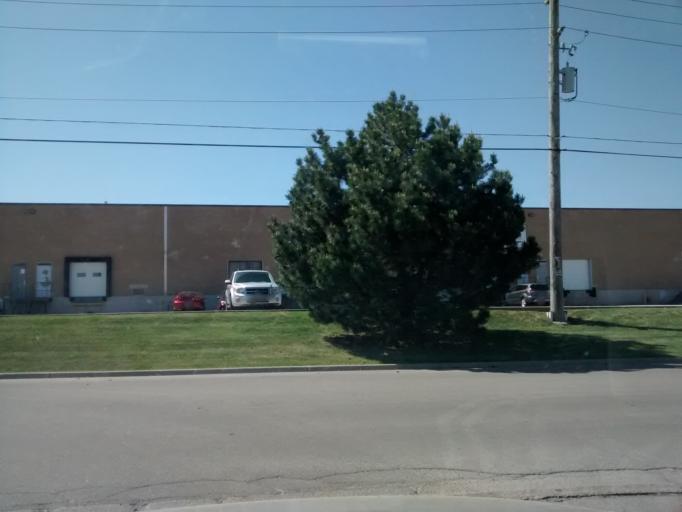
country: CA
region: Ontario
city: Burlington
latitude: 43.3571
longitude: -79.8077
